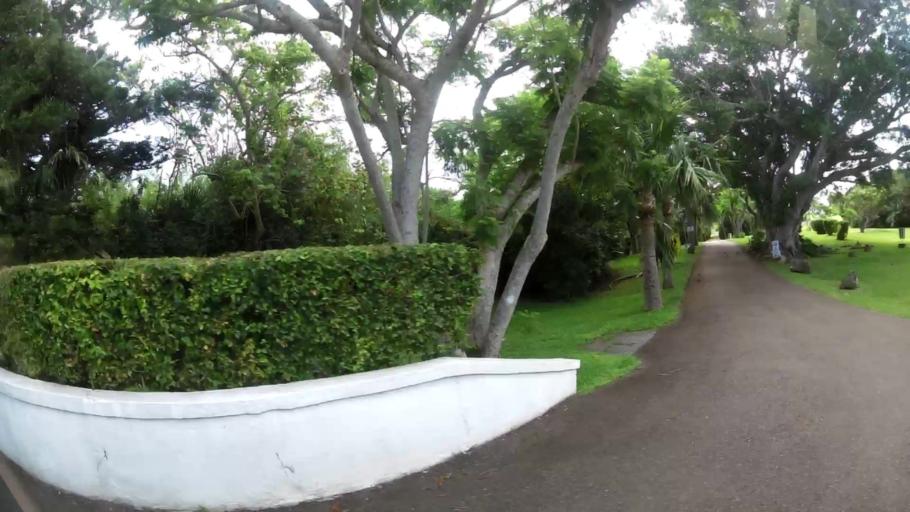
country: BM
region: Saint George
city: Saint George
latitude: 32.3719
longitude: -64.6980
